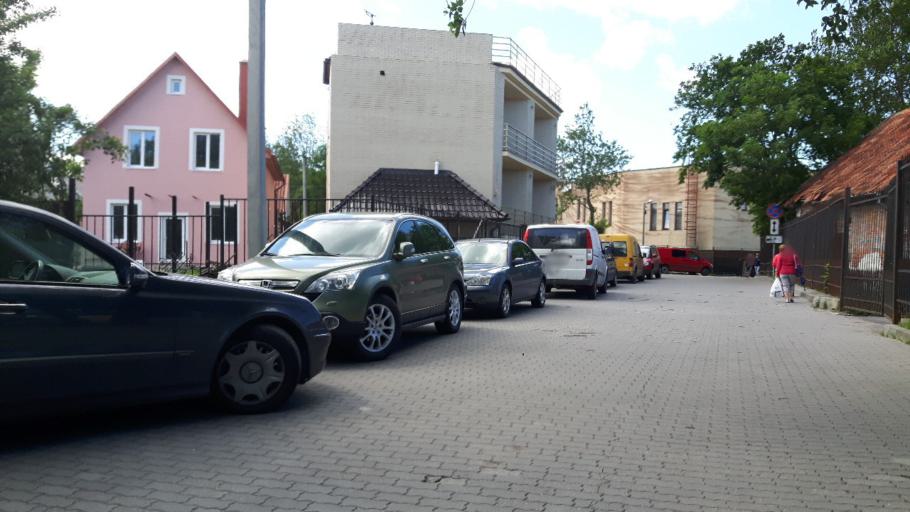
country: RU
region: Kaliningrad
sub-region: Zelenogradskiy Rayon
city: Zelenogradsk
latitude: 54.9604
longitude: 20.4722
